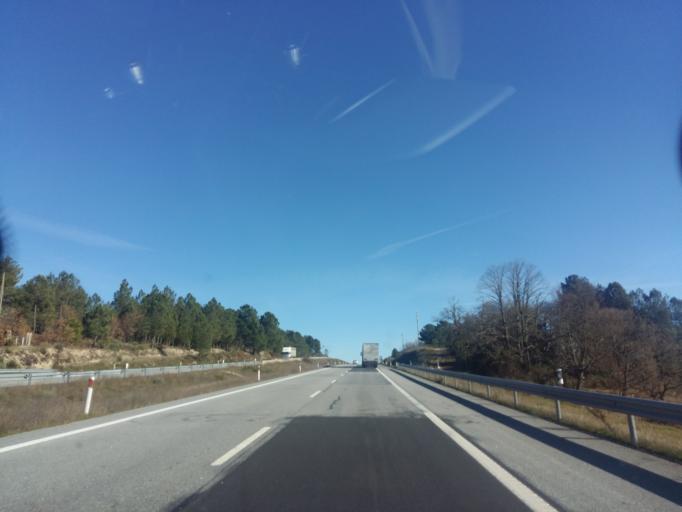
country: PT
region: Guarda
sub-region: Guarda
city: Sequeira
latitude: 40.5801
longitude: -7.1739
